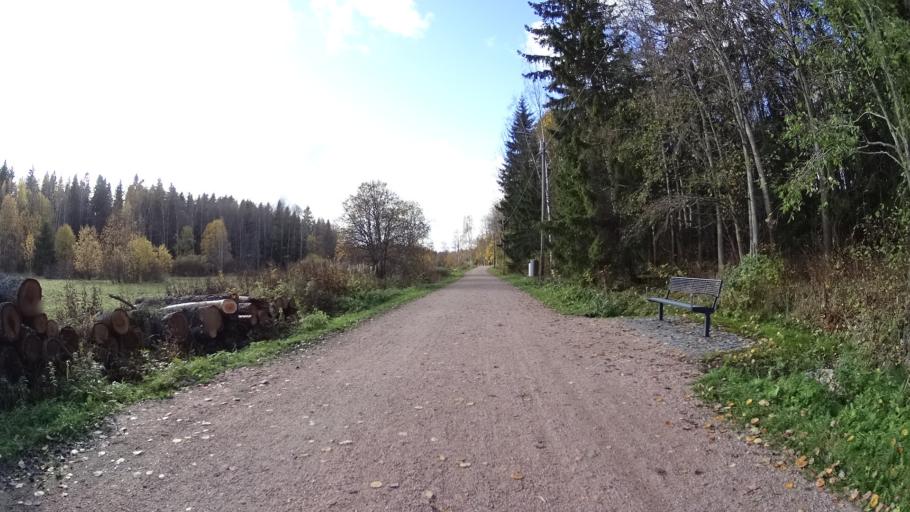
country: FI
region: Uusimaa
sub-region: Helsinki
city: Kilo
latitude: 60.2754
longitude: 24.8246
